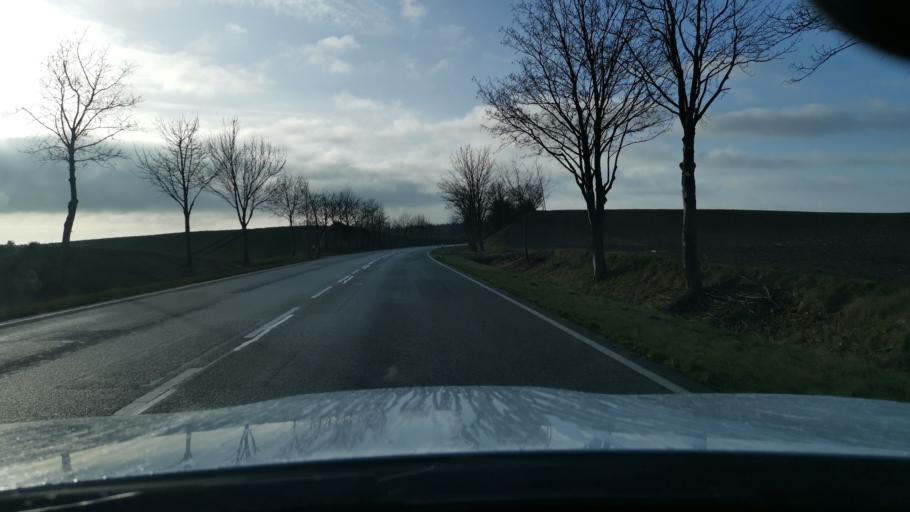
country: DE
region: Mecklenburg-Vorpommern
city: Laage
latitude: 53.9182
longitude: 12.3173
